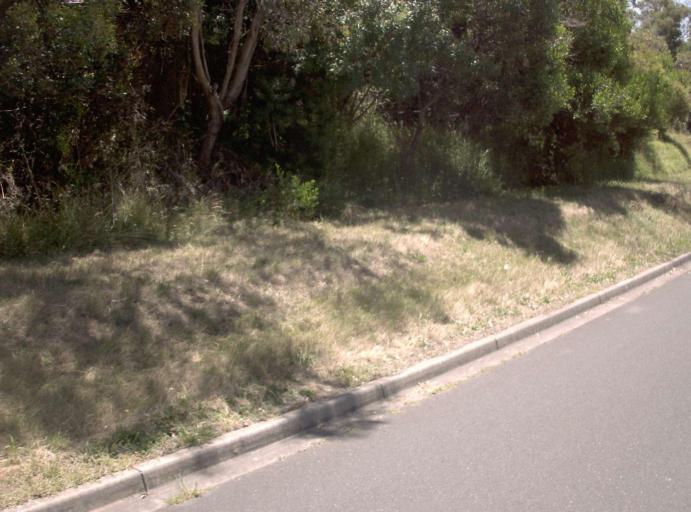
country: AU
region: Victoria
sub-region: Mornington Peninsula
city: Mount Eliza
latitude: -38.1844
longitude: 145.0969
